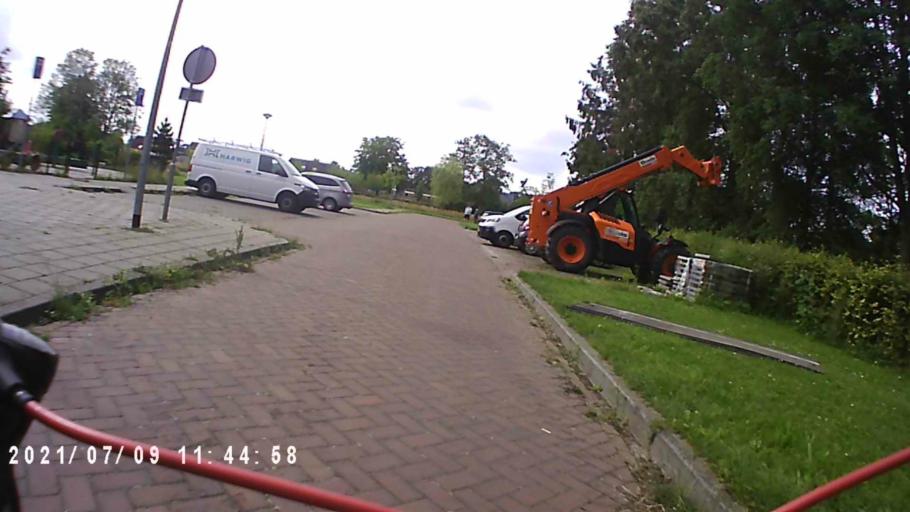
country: NL
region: Groningen
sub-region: Gemeente Slochteren
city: Slochteren
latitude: 53.1969
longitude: 6.8745
